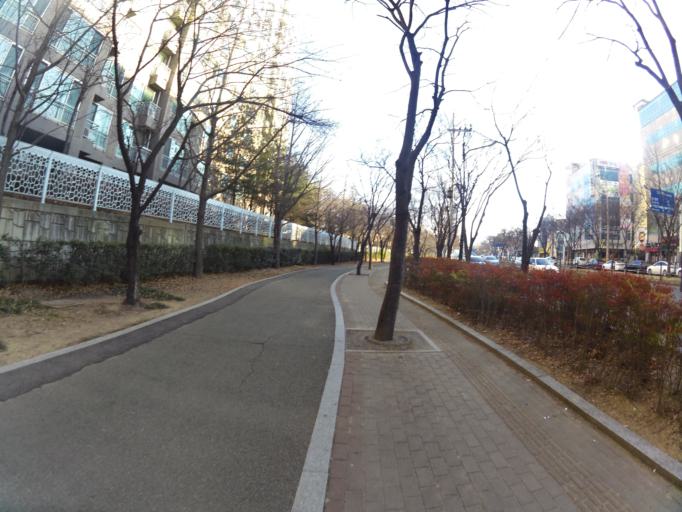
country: KR
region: Daegu
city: Daegu
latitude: 35.8681
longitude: 128.6384
